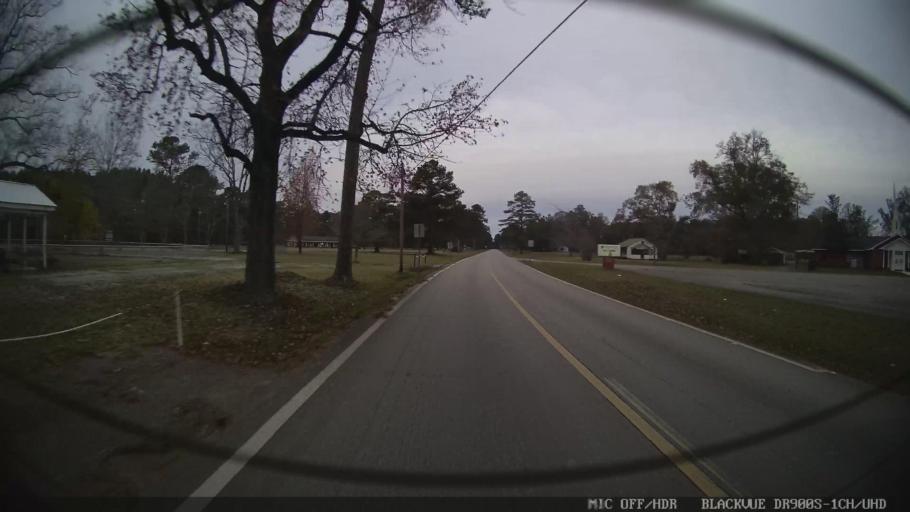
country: US
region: Mississippi
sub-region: Clarke County
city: Stonewall
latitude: 32.0418
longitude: -88.8882
